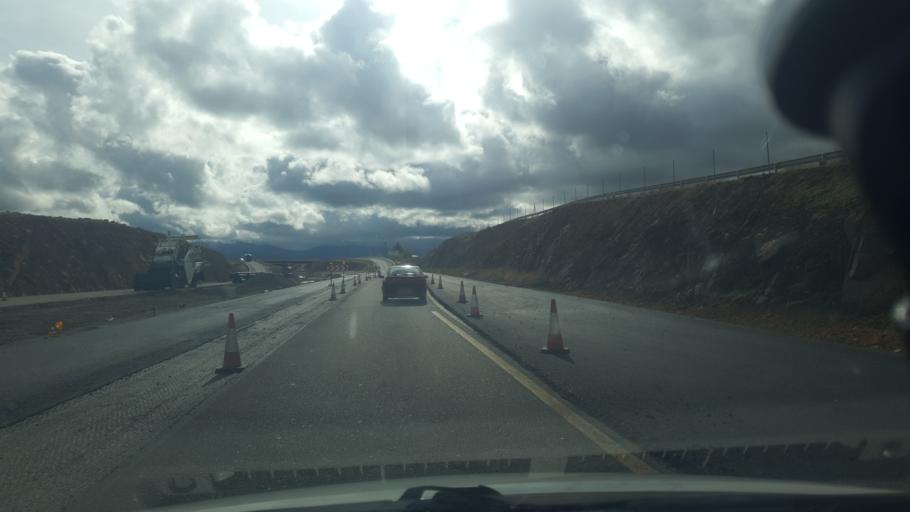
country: ES
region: Castille and Leon
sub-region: Provincia de Segovia
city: San Cristobal de Segovia
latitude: 40.9567
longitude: -4.0898
